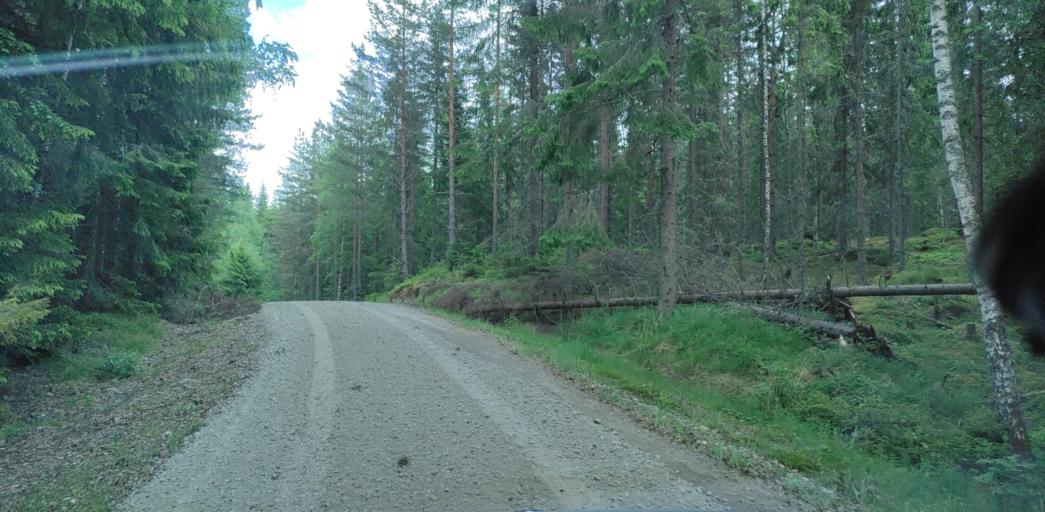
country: SE
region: Vaermland
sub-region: Munkfors Kommun
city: Munkfors
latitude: 59.9653
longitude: 13.4148
